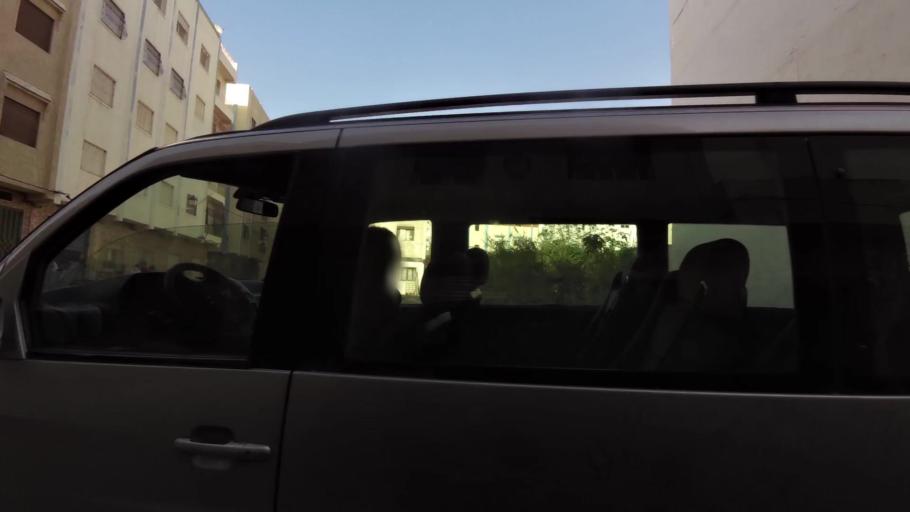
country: MA
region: Tanger-Tetouan
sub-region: Tetouan
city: Martil
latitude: 35.6276
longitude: -5.2802
